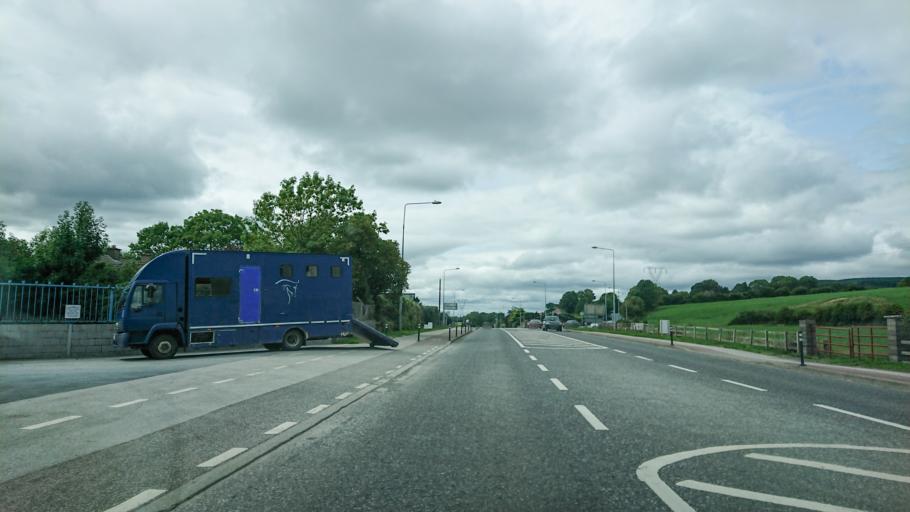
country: IE
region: Munster
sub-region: Waterford
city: Dungarvan
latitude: 52.1090
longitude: -7.6706
